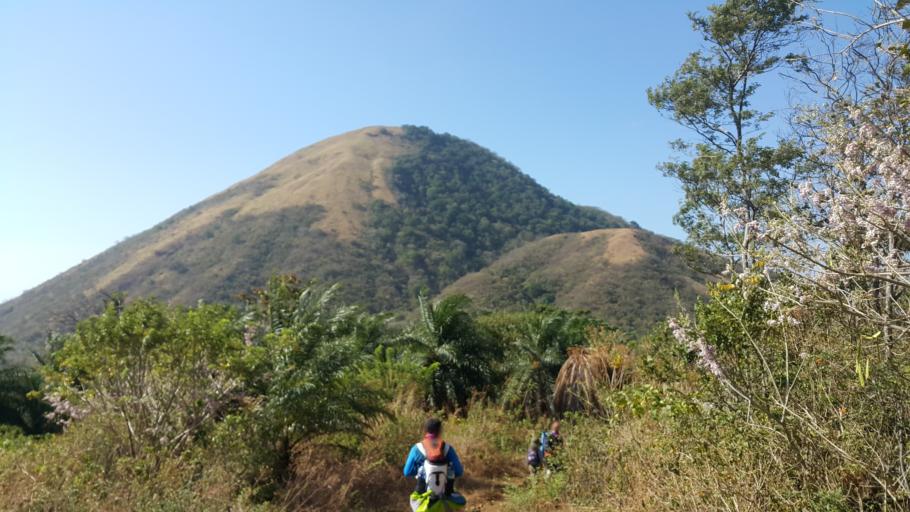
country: NI
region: Leon
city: La Paz Centro
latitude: 12.4672
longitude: -86.6754
